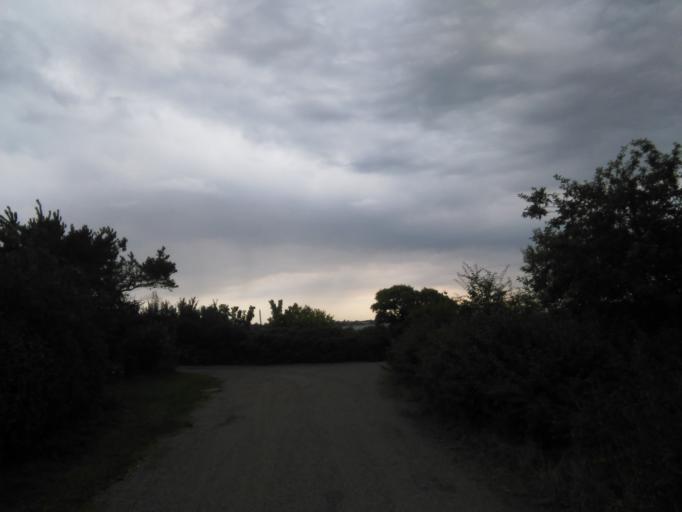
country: DK
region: Central Jutland
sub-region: Arhus Kommune
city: Hjortshoj
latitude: 56.2191
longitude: 10.2973
